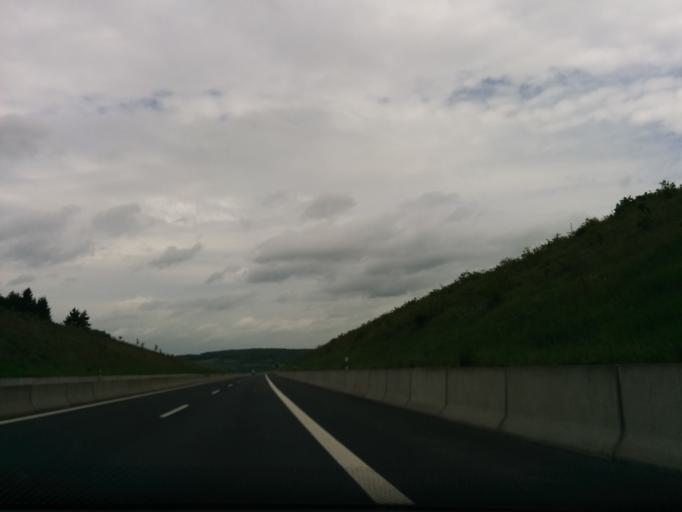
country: DE
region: Bavaria
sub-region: Regierungsbezirk Unterfranken
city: Munnerstadt
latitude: 50.2253
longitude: 10.2190
